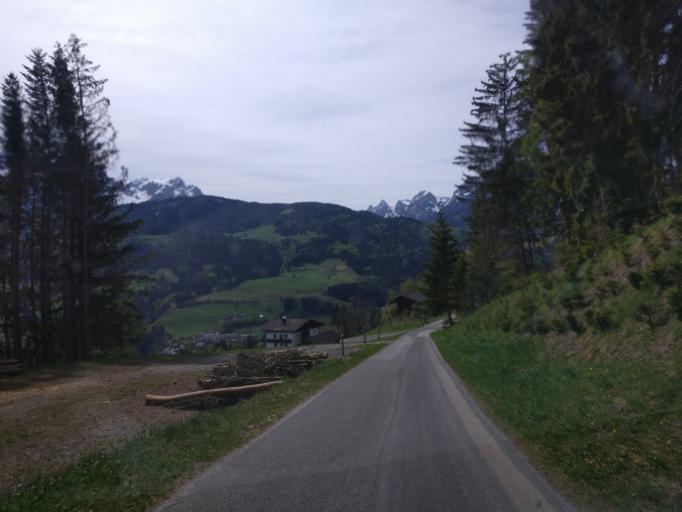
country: AT
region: Salzburg
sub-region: Politischer Bezirk Sankt Johann im Pongau
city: Pfarrwerfen
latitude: 47.4724
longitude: 13.2100
